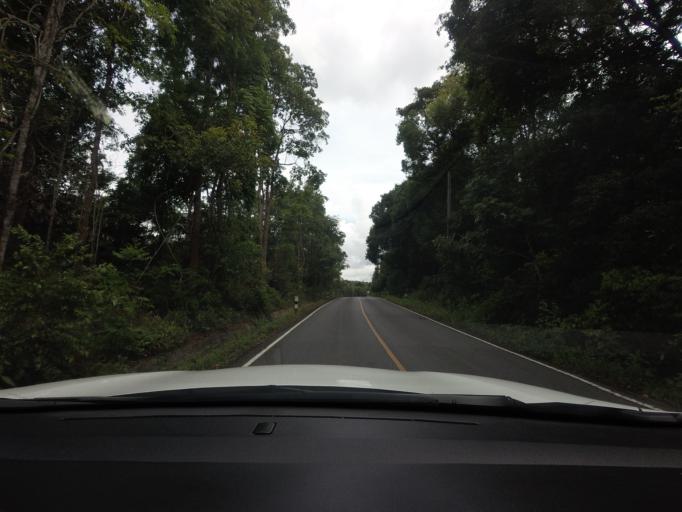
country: TH
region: Nakhon Nayok
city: Nakhon Nayok
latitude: 14.4249
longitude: 101.3711
